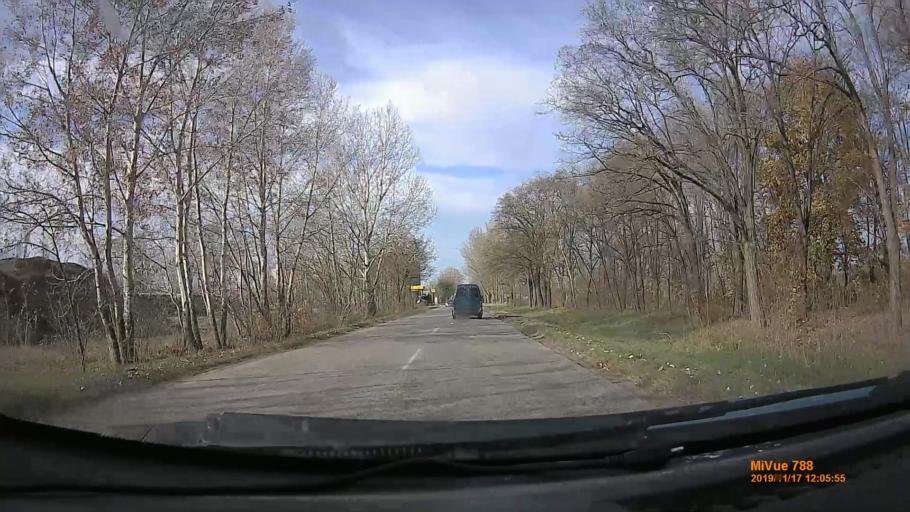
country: HU
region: Bacs-Kiskun
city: Szentkiraly
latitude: 46.9113
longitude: 19.9155
